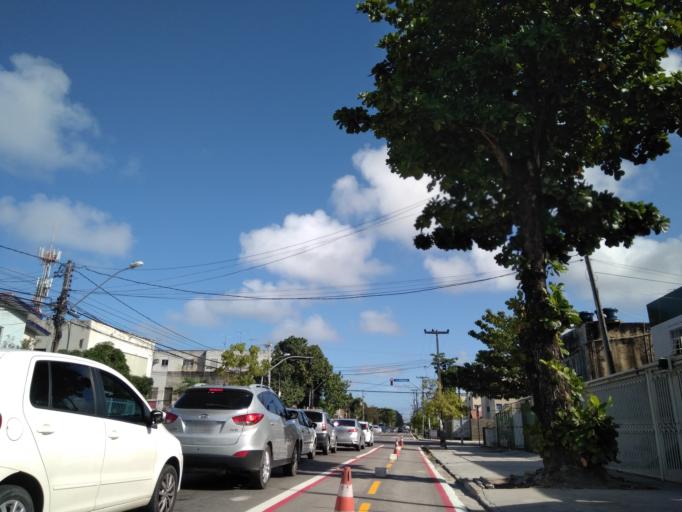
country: BR
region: Pernambuco
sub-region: Recife
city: Recife
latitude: -8.0905
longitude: -34.9106
